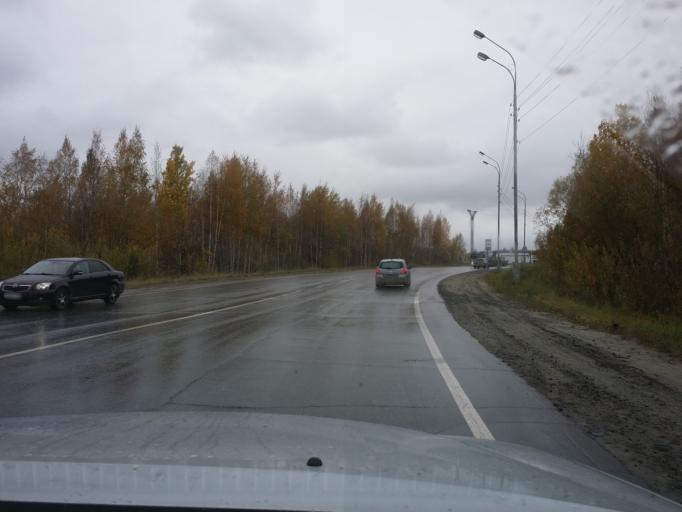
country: RU
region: Khanty-Mansiyskiy Avtonomnyy Okrug
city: Megion
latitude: 61.0480
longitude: 76.1130
